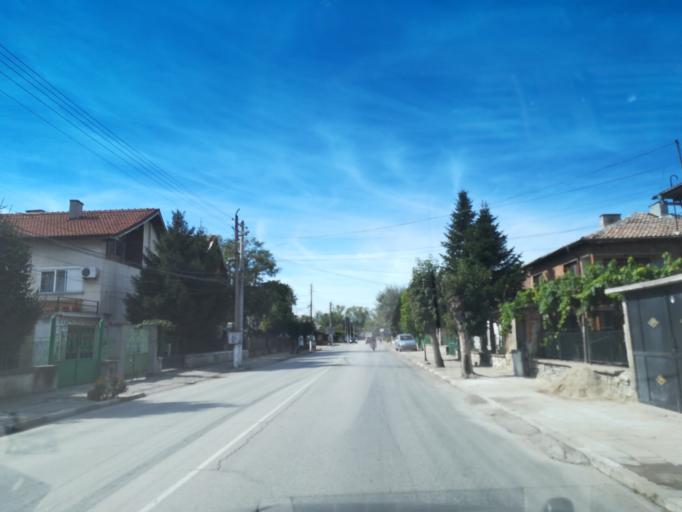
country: BG
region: Plovdiv
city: Stamboliyski
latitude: 42.1188
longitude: 24.5623
